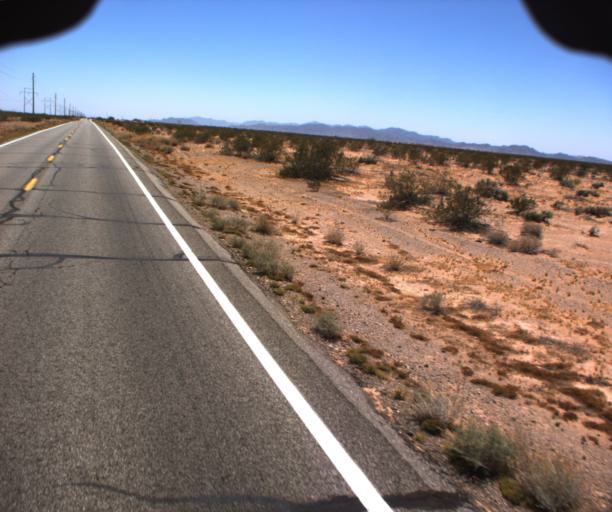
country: US
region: Arizona
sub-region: La Paz County
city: Quartzsite
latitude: 33.8682
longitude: -114.2170
